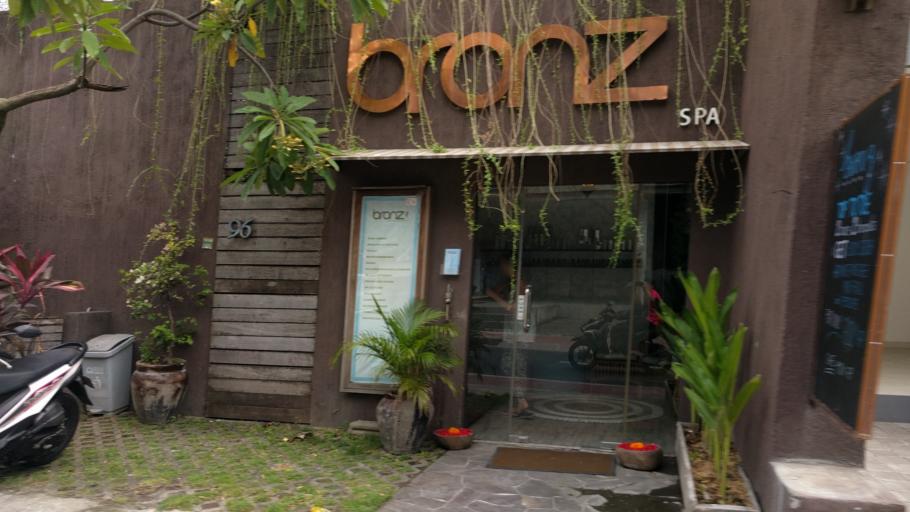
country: ID
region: Bali
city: Kuta
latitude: -8.6730
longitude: 115.1518
